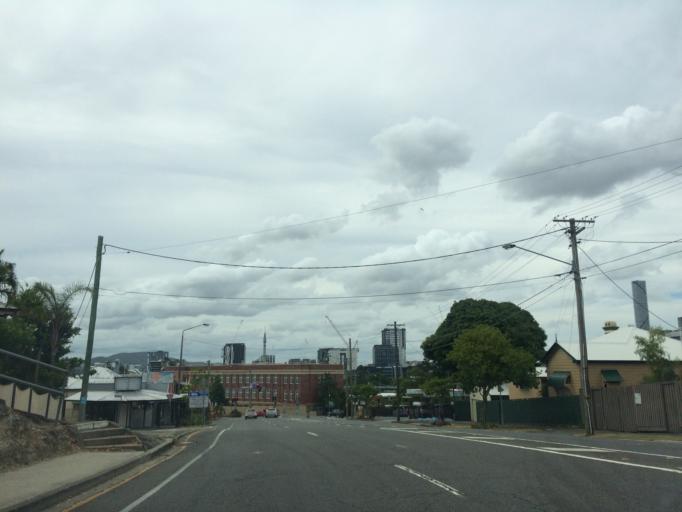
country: AU
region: Queensland
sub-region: Brisbane
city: South Brisbane
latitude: -27.4832
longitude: 153.0196
